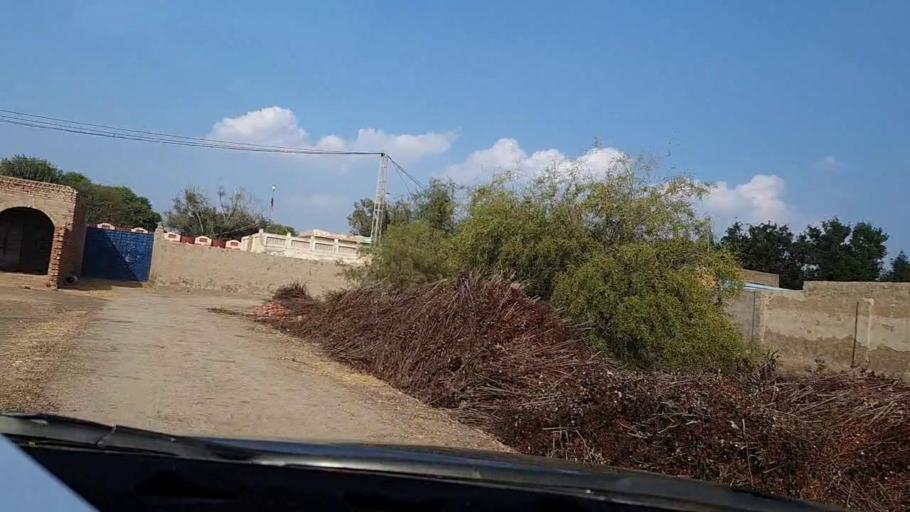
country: PK
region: Sindh
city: Nawabshah
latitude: 26.1691
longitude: 68.3644
